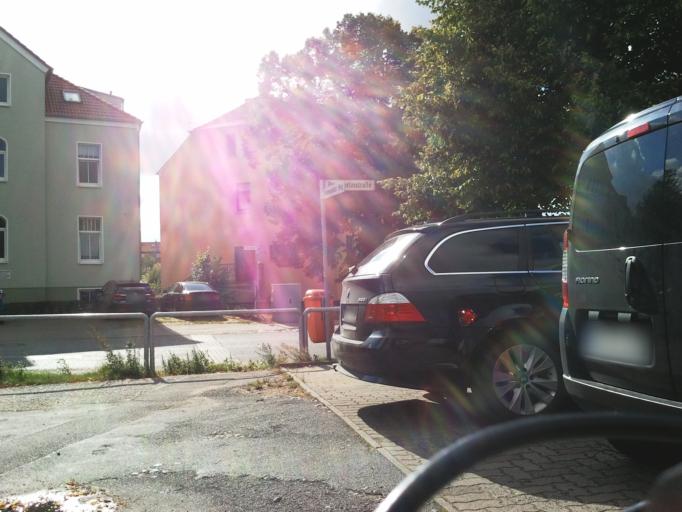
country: DE
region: Mecklenburg-Vorpommern
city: Rostock
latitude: 54.1039
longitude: 12.1153
